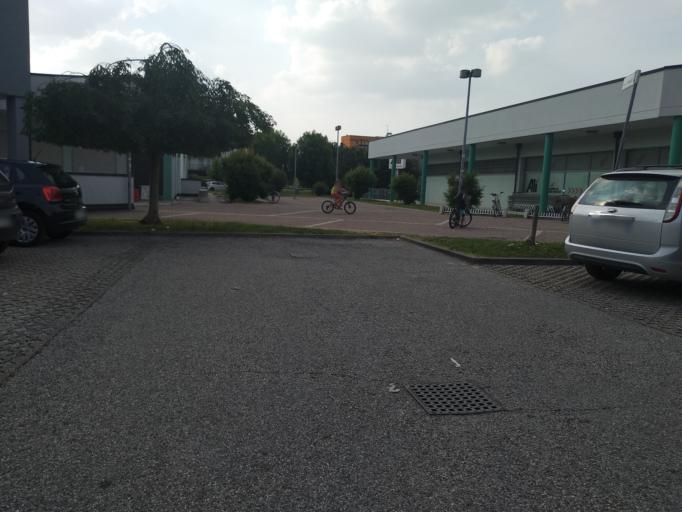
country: IT
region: Veneto
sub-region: Provincia di Padova
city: Sarmeola
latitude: 45.4257
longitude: 11.8450
